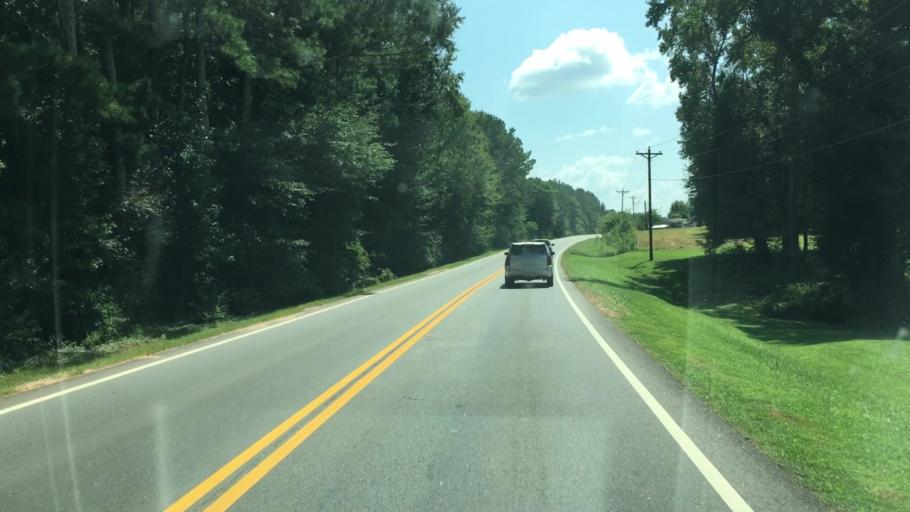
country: US
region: Georgia
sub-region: Oconee County
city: Watkinsville
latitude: 33.7819
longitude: -83.4235
